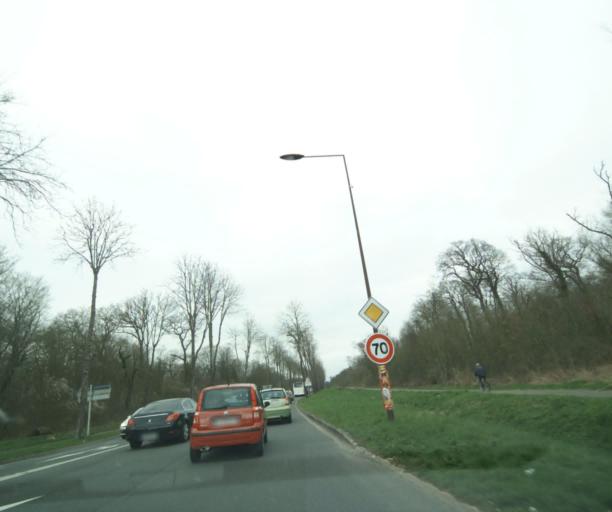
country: FR
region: Ile-de-France
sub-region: Departement des Yvelines
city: Saint-Germain-en-Laye
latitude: 48.9109
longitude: 2.0735
